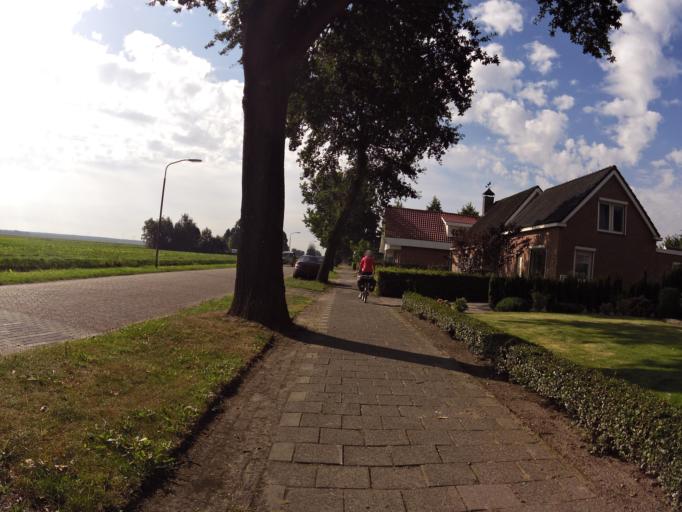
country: NL
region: Drenthe
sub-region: Gemeente Emmen
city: Klazienaveen
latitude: 52.7207
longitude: 7.0470
